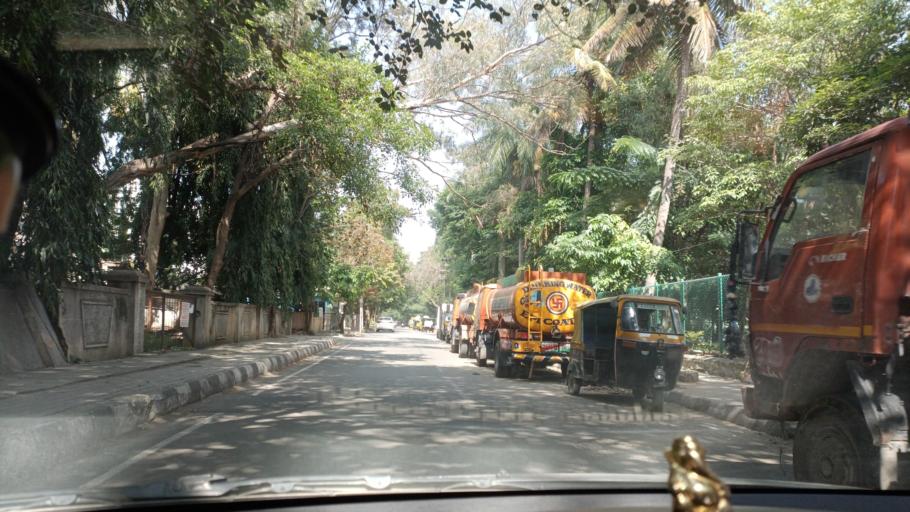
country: IN
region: Karnataka
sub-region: Bangalore Urban
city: Bangalore
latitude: 12.9105
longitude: 77.6155
